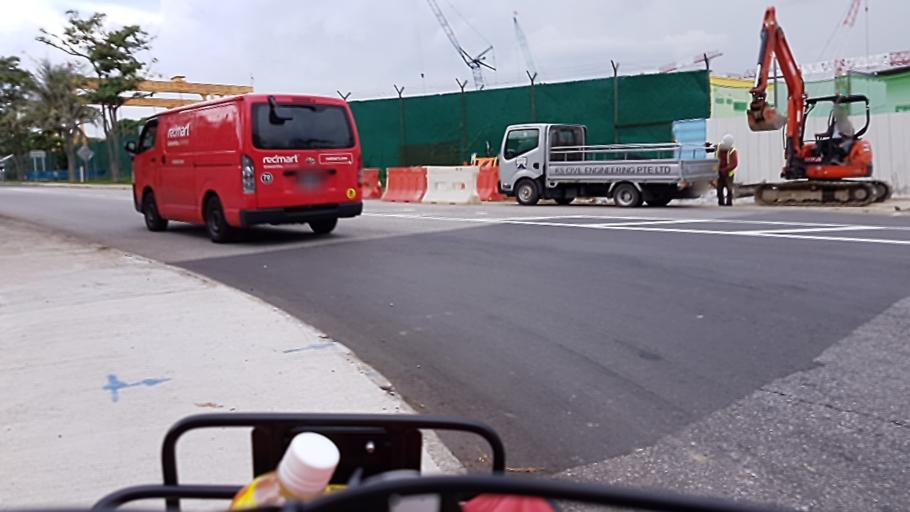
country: MY
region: Johor
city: Kampung Pasir Gudang Baru
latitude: 1.3693
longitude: 103.9789
